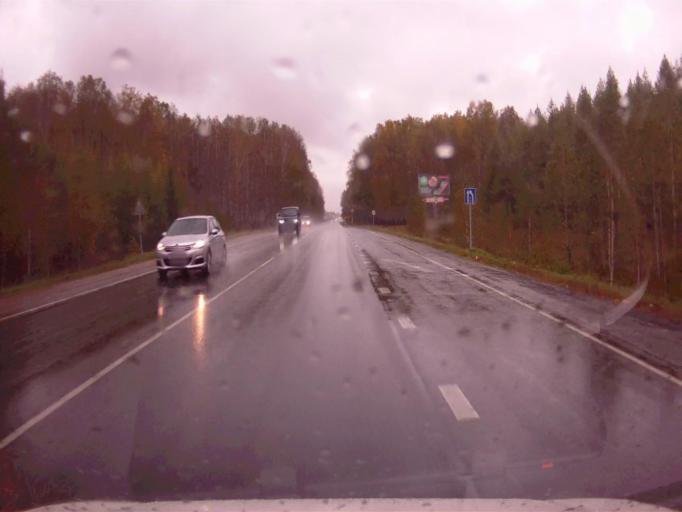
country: RU
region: Chelyabinsk
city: Argayash
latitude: 55.4130
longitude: 61.0367
